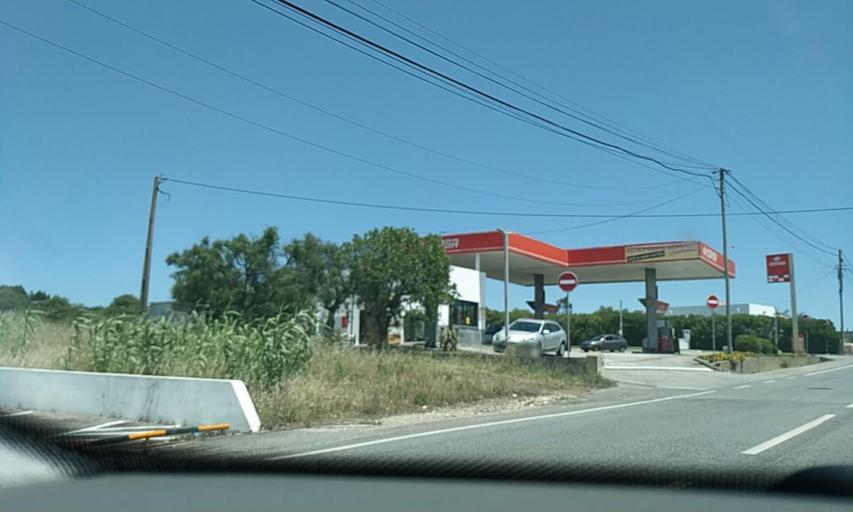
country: PT
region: Lisbon
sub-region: Sintra
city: Almargem
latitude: 38.8773
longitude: -9.2699
